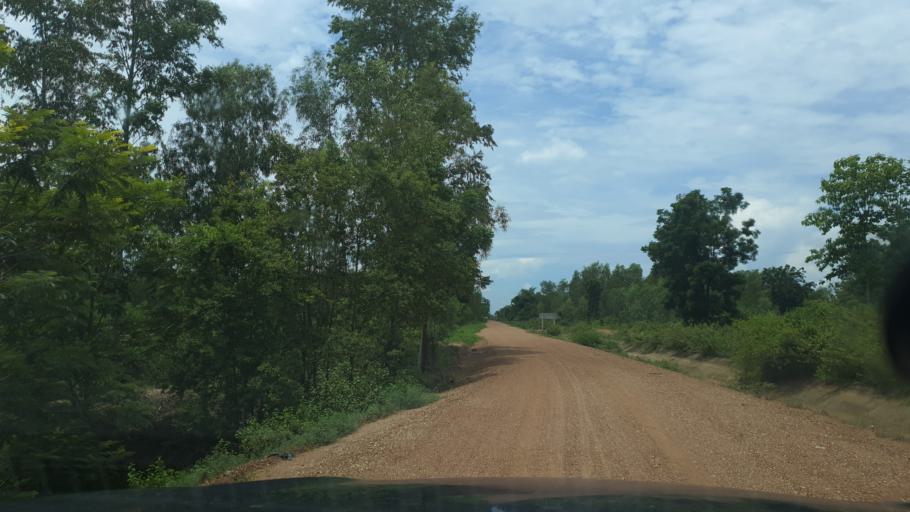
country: TH
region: Lampang
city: Hang Chat
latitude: 18.2774
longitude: 99.3723
